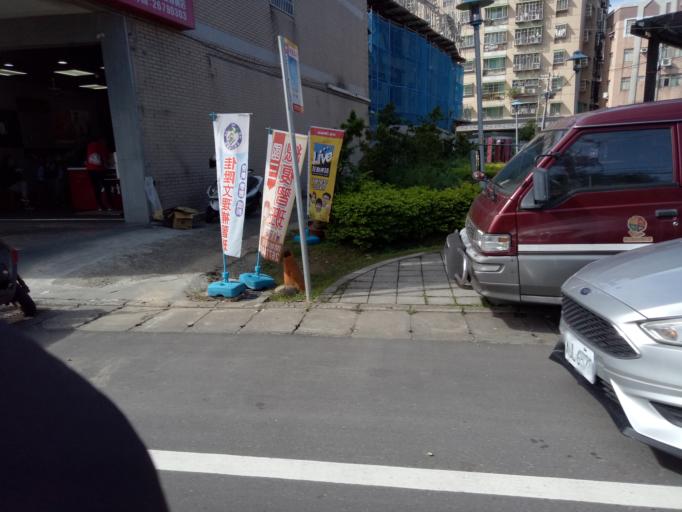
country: TW
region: Taiwan
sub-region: Taoyuan
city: Taoyuan
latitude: 24.9416
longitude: 121.3388
